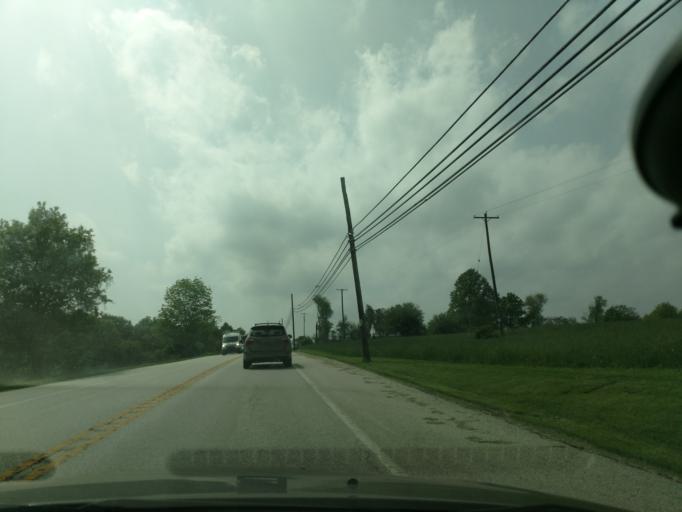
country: US
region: Pennsylvania
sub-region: Montgomery County
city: Stowe
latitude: 40.1741
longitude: -75.7003
